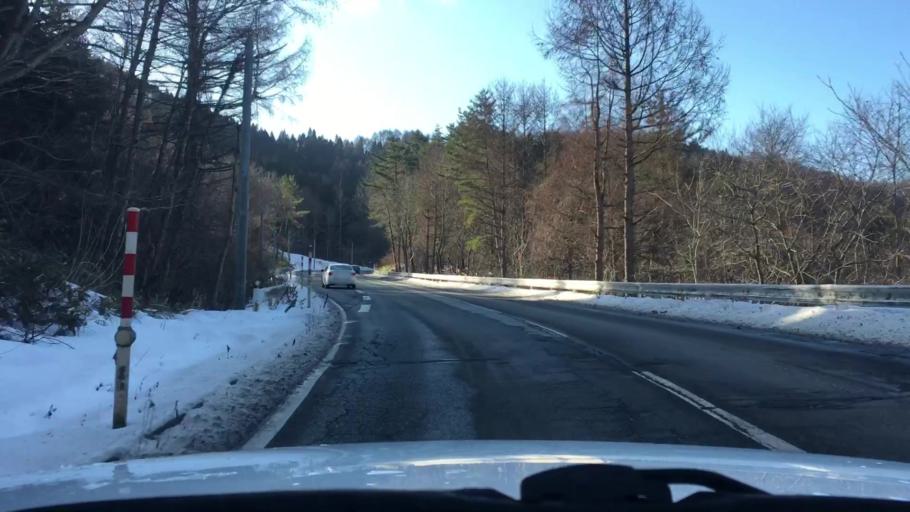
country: JP
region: Iwate
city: Morioka-shi
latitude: 39.6686
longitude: 141.3323
